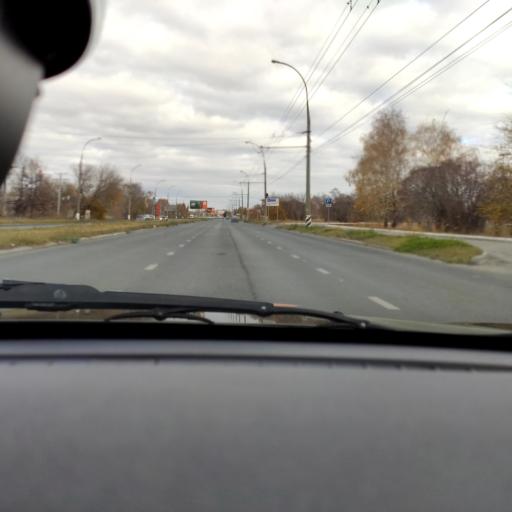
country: RU
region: Samara
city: Tol'yatti
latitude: 53.5437
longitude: 49.3011
